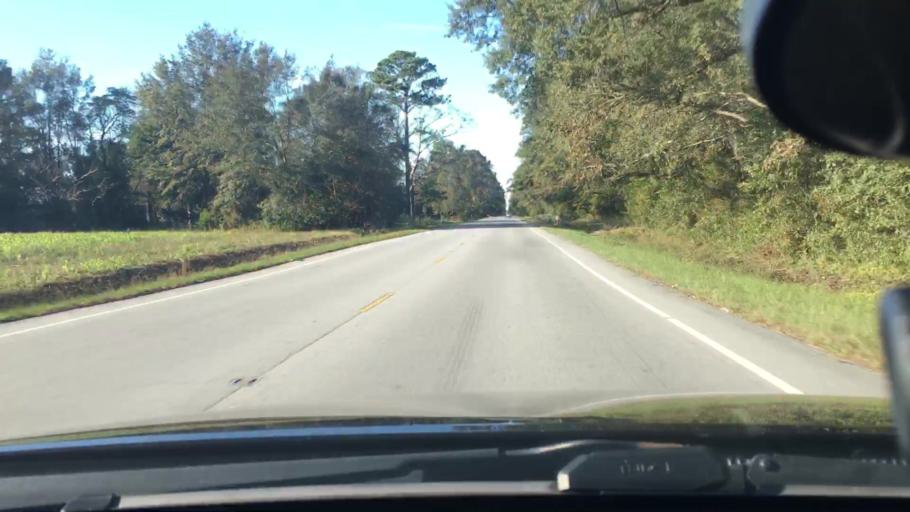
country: US
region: North Carolina
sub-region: Craven County
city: New Bern
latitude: 35.1792
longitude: -77.0469
